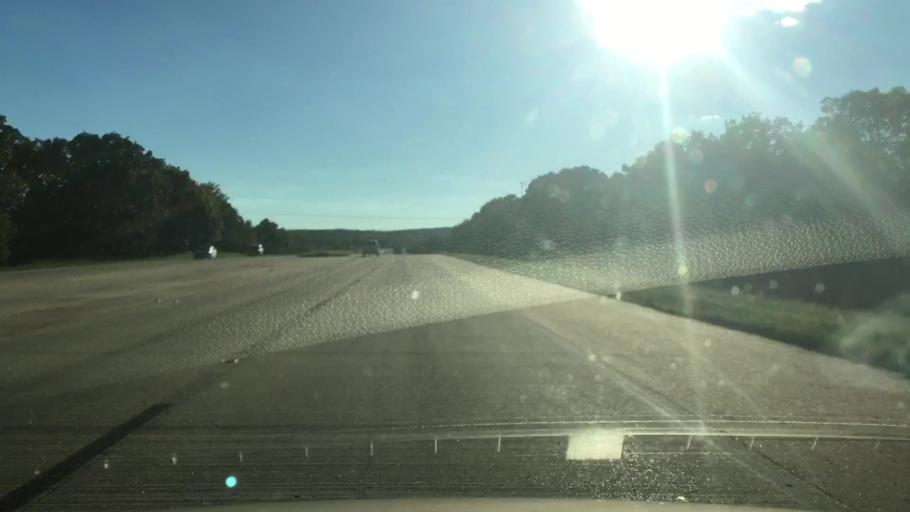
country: US
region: Oklahoma
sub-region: Cherokee County
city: Park Hill
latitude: 35.8147
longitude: -95.0626
